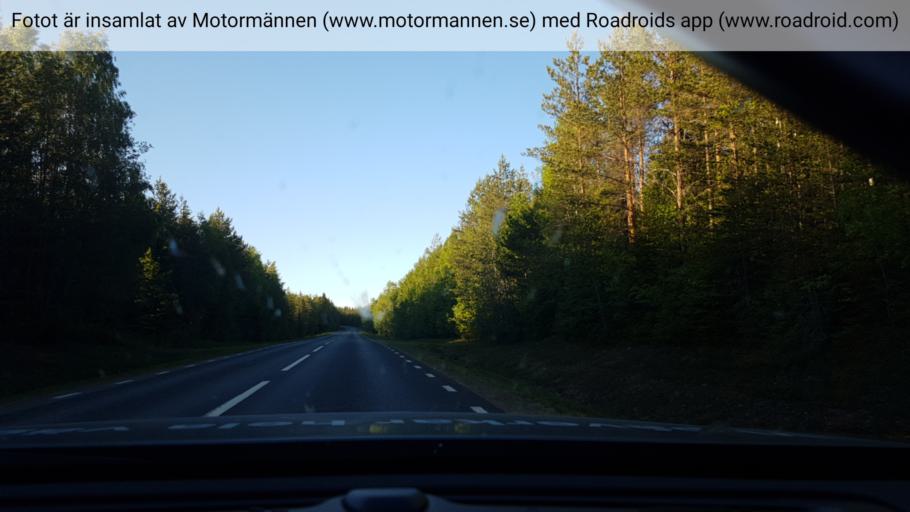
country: SE
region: Vaesterbotten
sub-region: Nordmalings Kommun
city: Nordmaling
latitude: 63.7214
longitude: 19.6428
